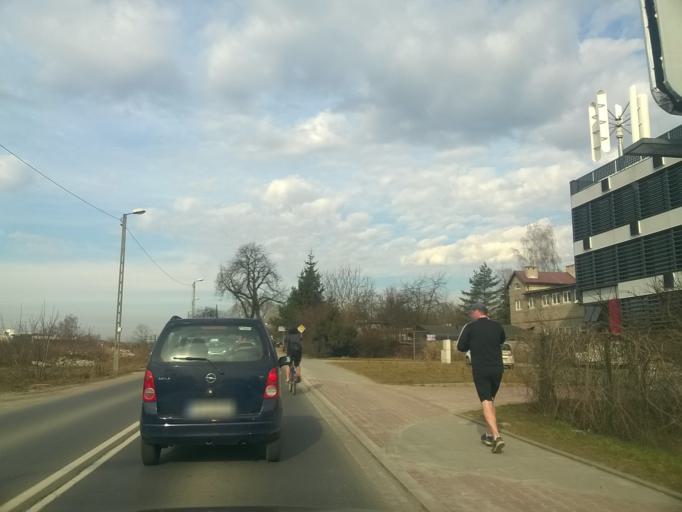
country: PL
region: Lesser Poland Voivodeship
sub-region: Powiat krakowski
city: Rzaska
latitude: 50.0809
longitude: 19.8694
